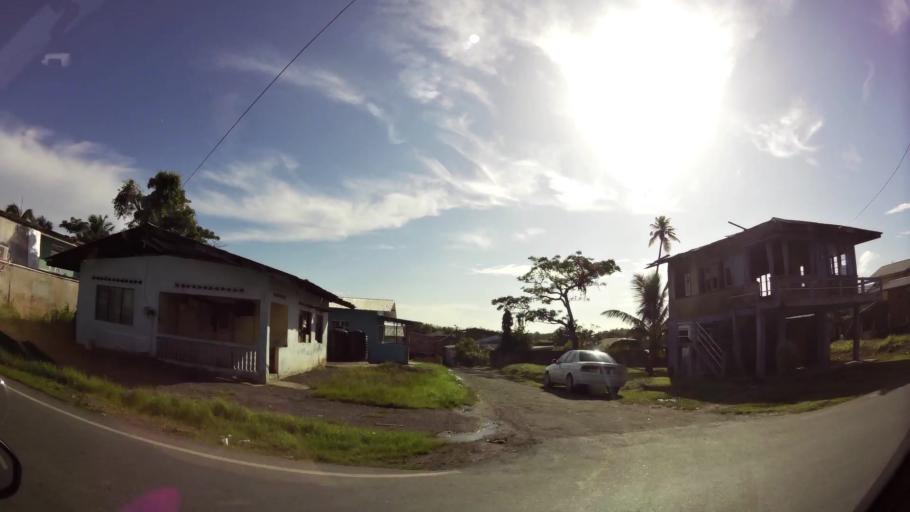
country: TT
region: Chaguanas
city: Chaguanas
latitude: 10.5169
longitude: -61.3789
